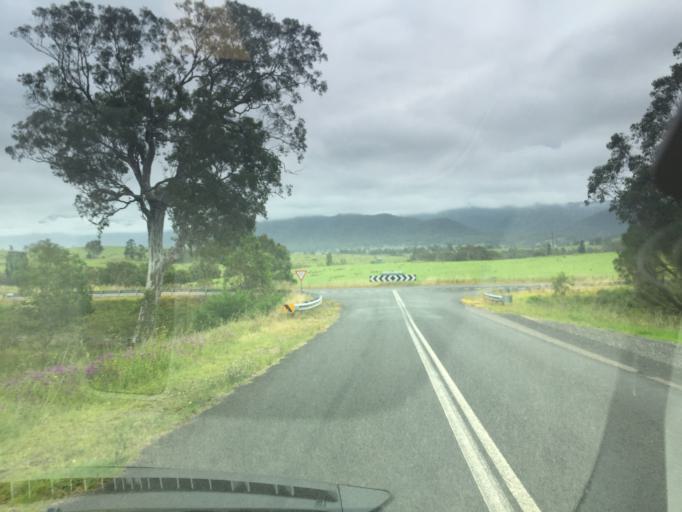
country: AU
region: New South Wales
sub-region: Bega Valley
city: Bega
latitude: -36.6449
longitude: 149.5866
